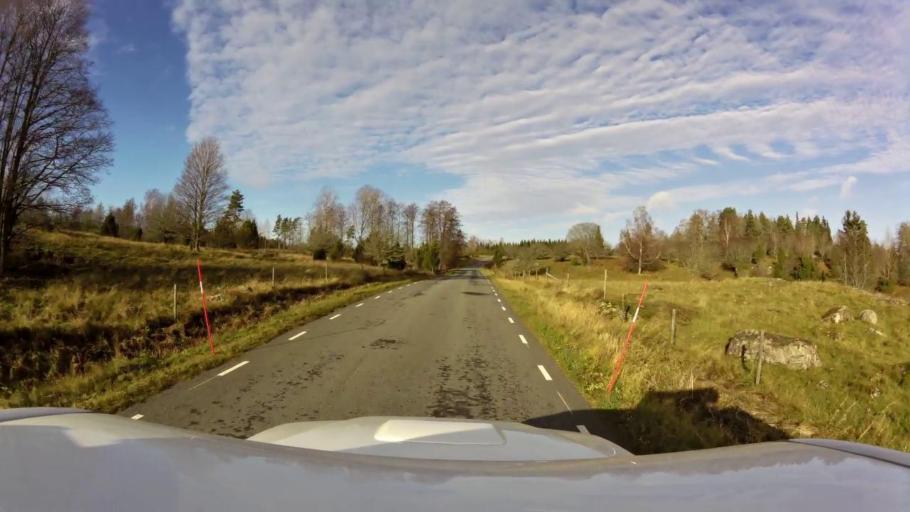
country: SE
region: OEstergoetland
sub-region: Linkopings Kommun
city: Sturefors
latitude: 58.2665
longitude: 15.6663
